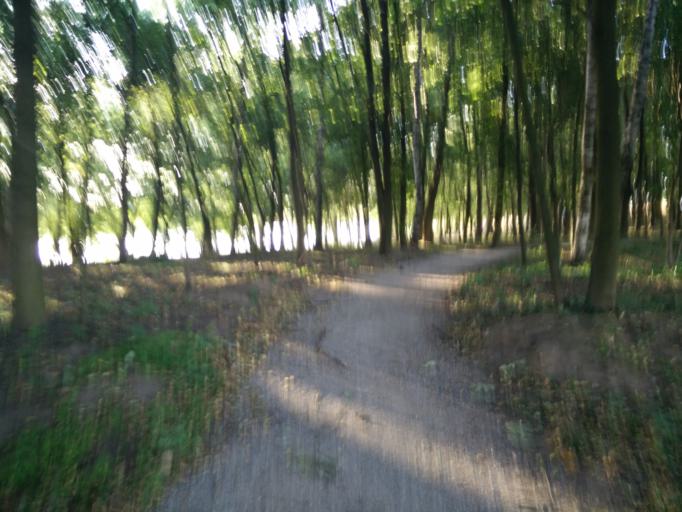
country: PL
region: Greater Poland Voivodeship
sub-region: Powiat sredzki
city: Sroda Wielkopolska
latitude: 52.2387
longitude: 17.2939
